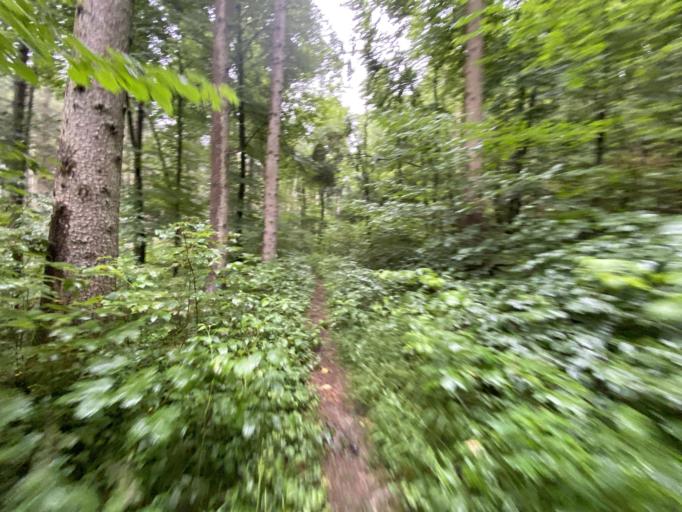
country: DE
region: Baden-Wuerttemberg
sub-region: Tuebingen Region
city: Bingen
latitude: 48.1145
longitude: 9.2628
